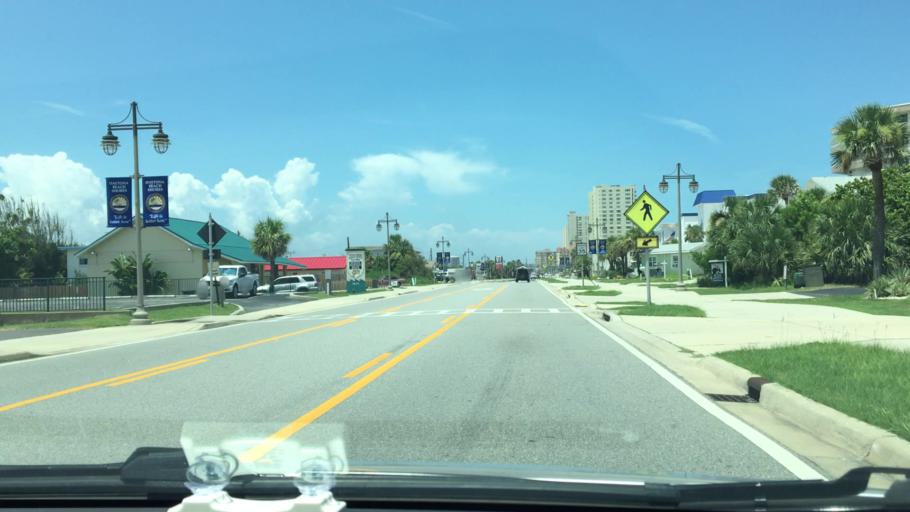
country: US
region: Florida
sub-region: Volusia County
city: Port Orange
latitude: 29.1465
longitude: -80.9667
